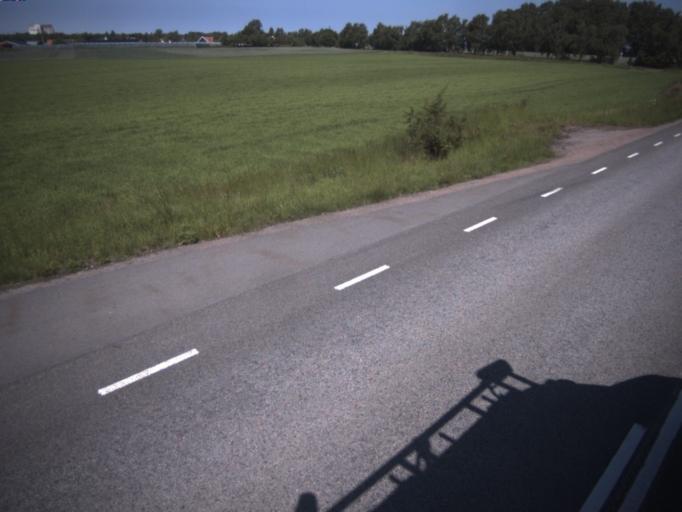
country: SE
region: Skane
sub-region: Helsingborg
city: Barslov
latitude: 56.0130
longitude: 12.7946
